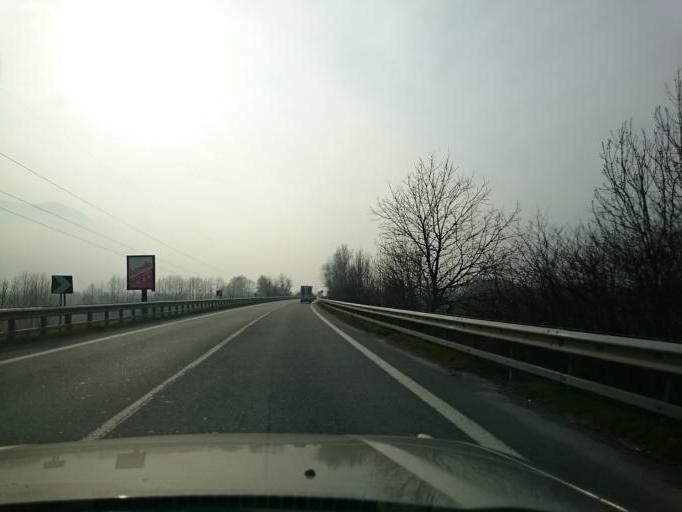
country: IT
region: Lombardy
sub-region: Provincia di Brescia
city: Artogne
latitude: 45.8604
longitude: 10.1538
